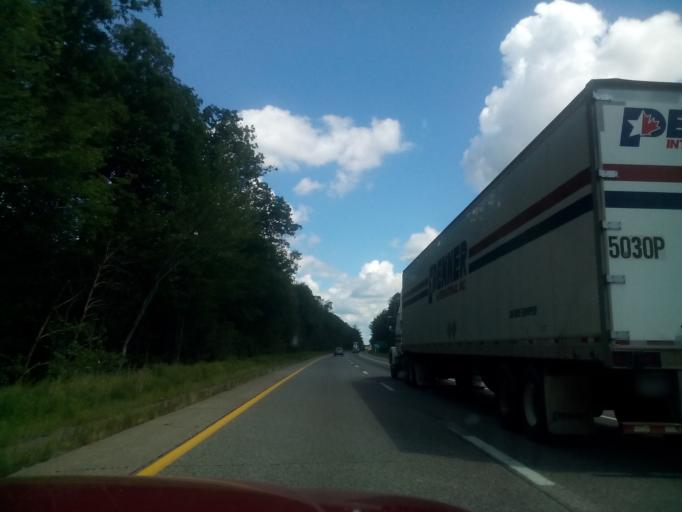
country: US
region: Pennsylvania
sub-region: Luzerne County
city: Conyngham
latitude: 41.0328
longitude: -76.0637
